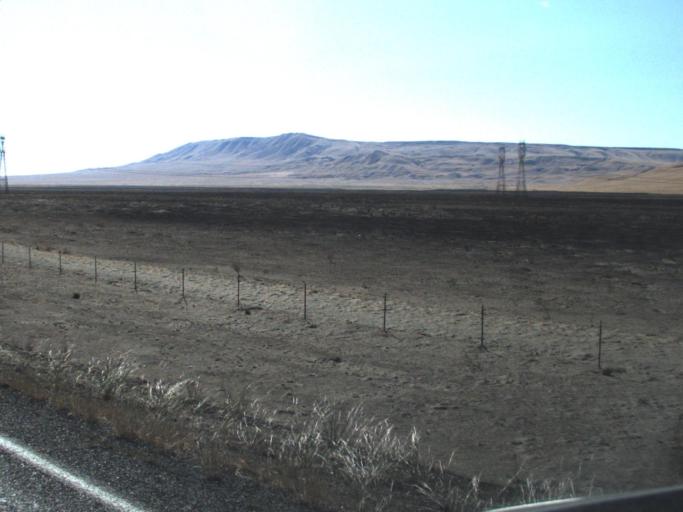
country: US
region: Washington
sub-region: Grant County
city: Desert Aire
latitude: 46.5644
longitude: -119.7169
